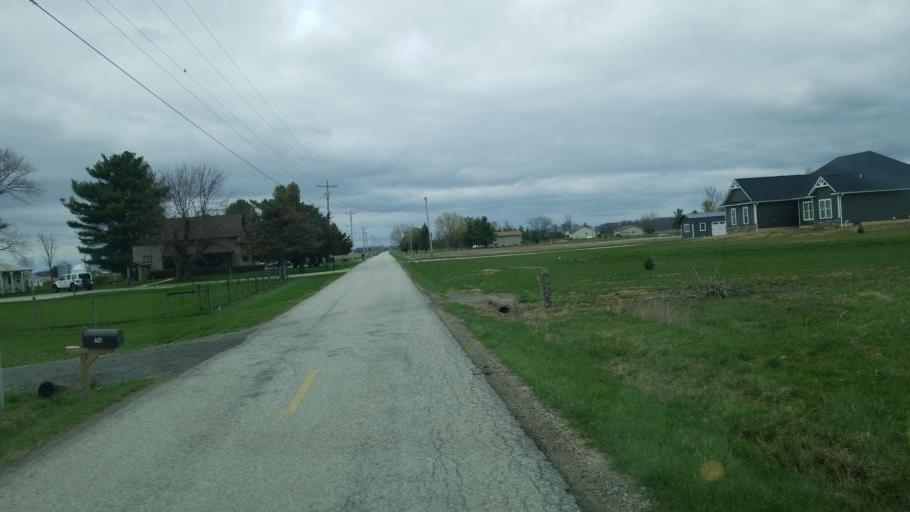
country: US
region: Ohio
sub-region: Delaware County
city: Delaware
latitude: 40.3797
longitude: -83.1192
